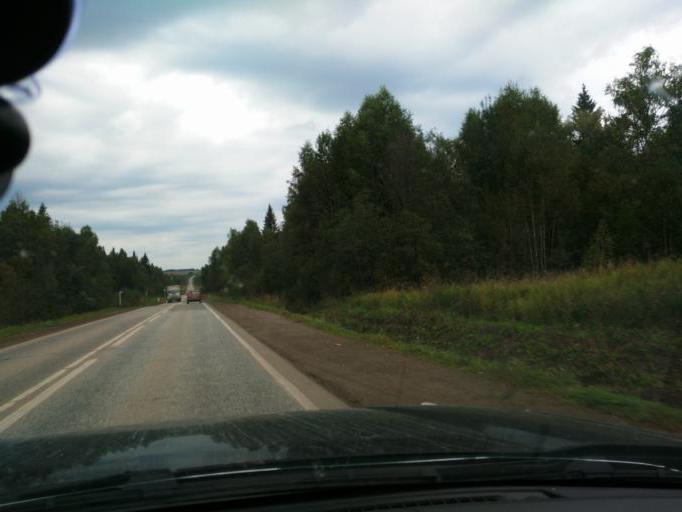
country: RU
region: Perm
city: Chernushka
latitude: 56.8009
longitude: 56.0690
